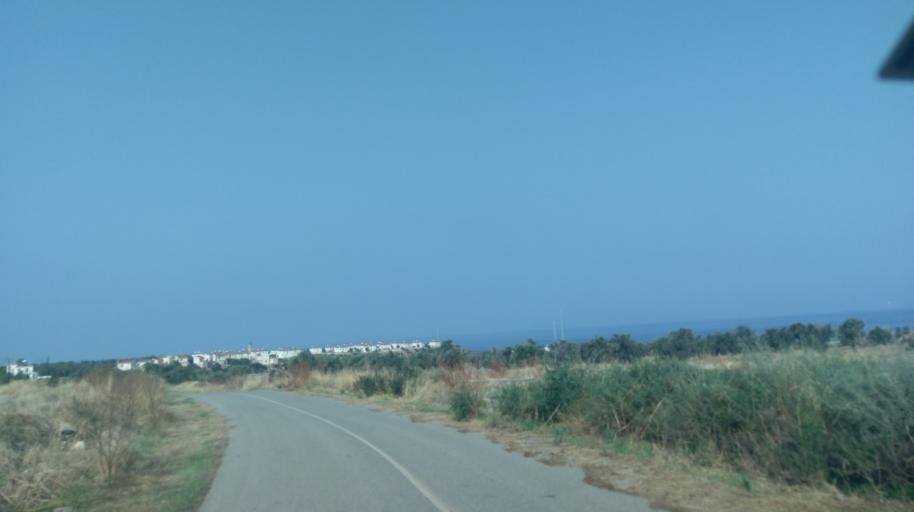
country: CY
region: Keryneia
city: Kyrenia
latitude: 35.3220
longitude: 33.4693
